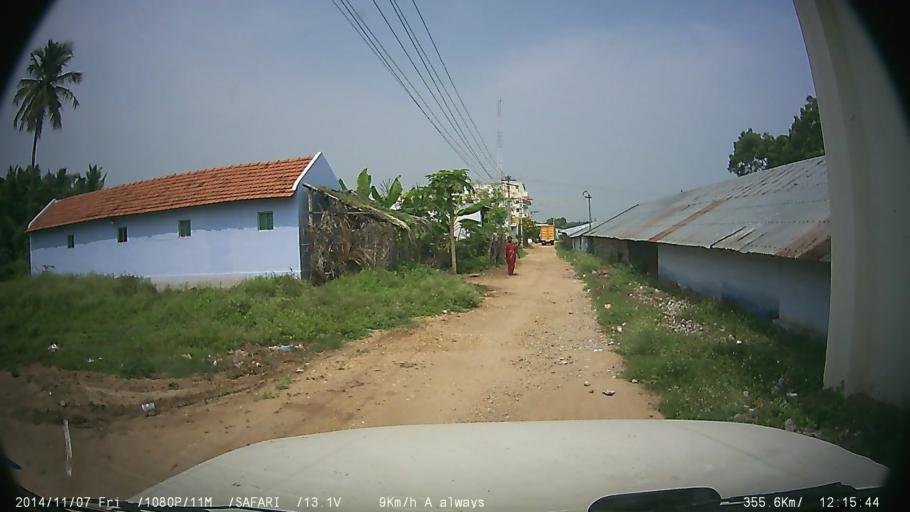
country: IN
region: Tamil Nadu
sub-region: Tiruppur
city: Tiruppur
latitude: 11.1017
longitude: 77.2897
